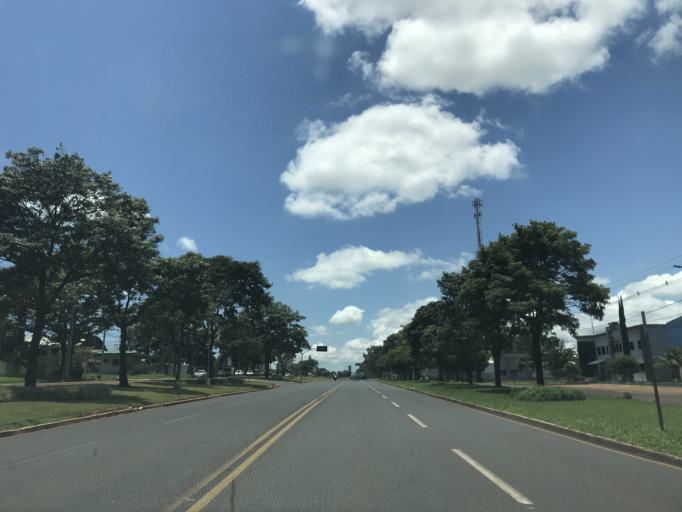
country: BR
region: Parana
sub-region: Marialva
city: Marialva
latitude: -23.4740
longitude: -51.8152
